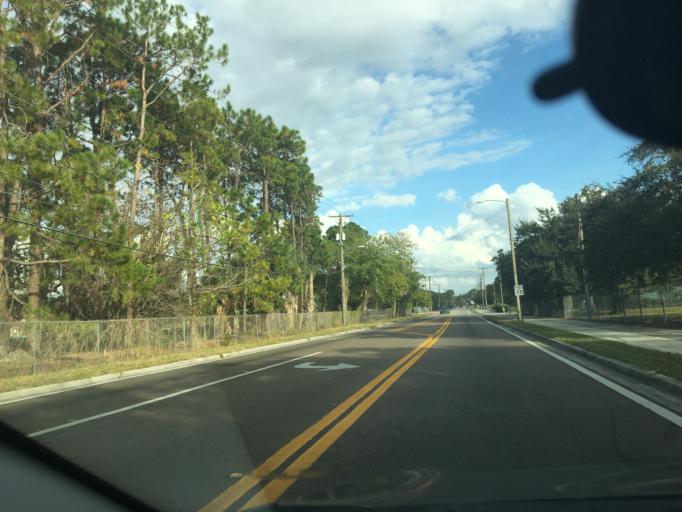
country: US
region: Florida
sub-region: Hillsborough County
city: Temple Terrace
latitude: 28.0435
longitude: -82.4159
